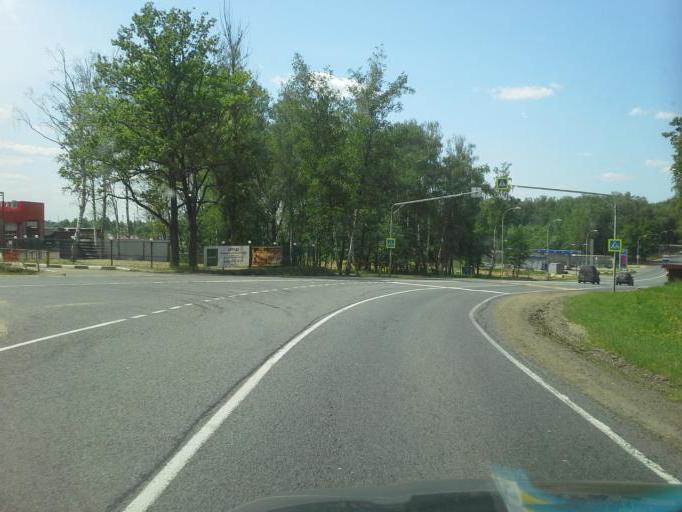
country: RU
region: Moskovskaya
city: Odintsovo
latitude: 55.6959
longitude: 37.2312
